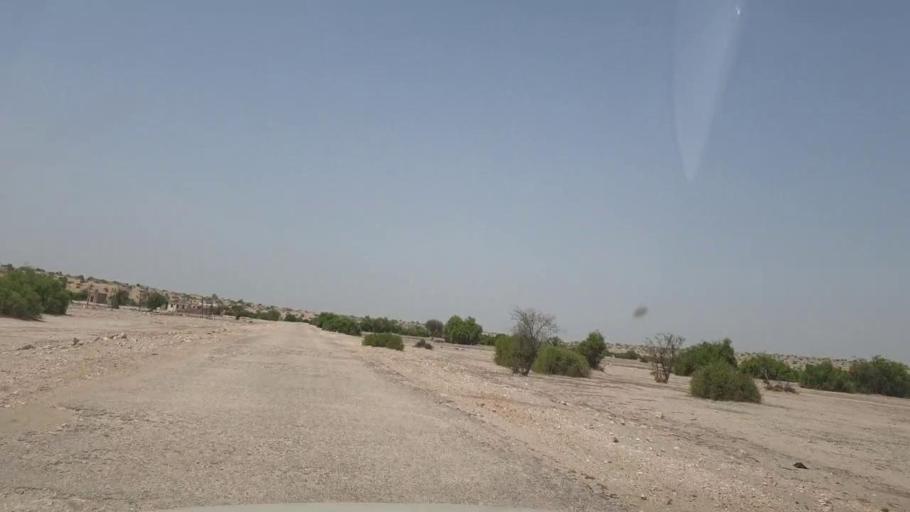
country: PK
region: Sindh
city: Khanpur
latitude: 27.3326
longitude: 69.3055
